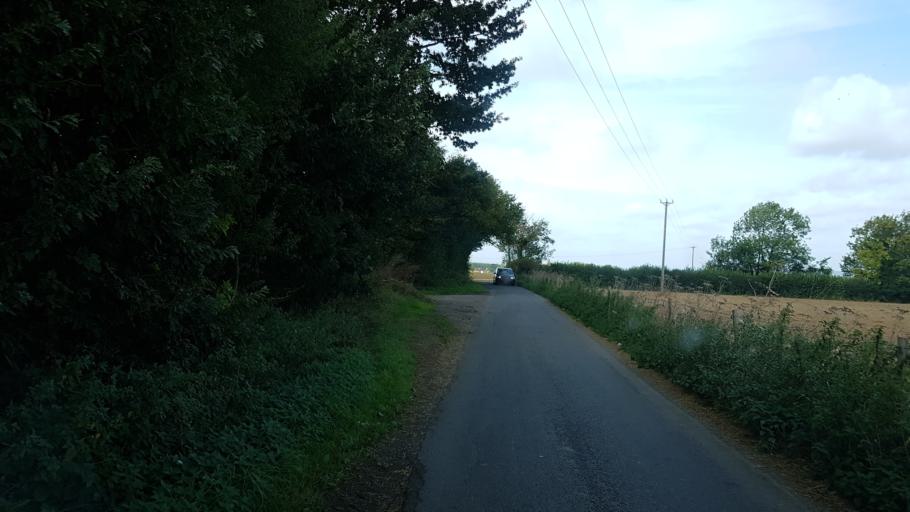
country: GB
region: England
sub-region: Kent
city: Harrietsham
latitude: 51.2401
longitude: 0.6179
